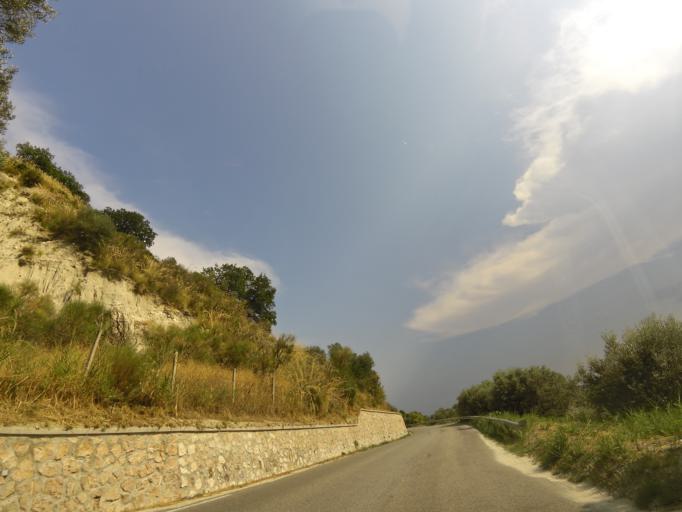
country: IT
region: Calabria
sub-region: Provincia di Reggio Calabria
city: Monasterace
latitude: 38.4611
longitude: 16.5204
